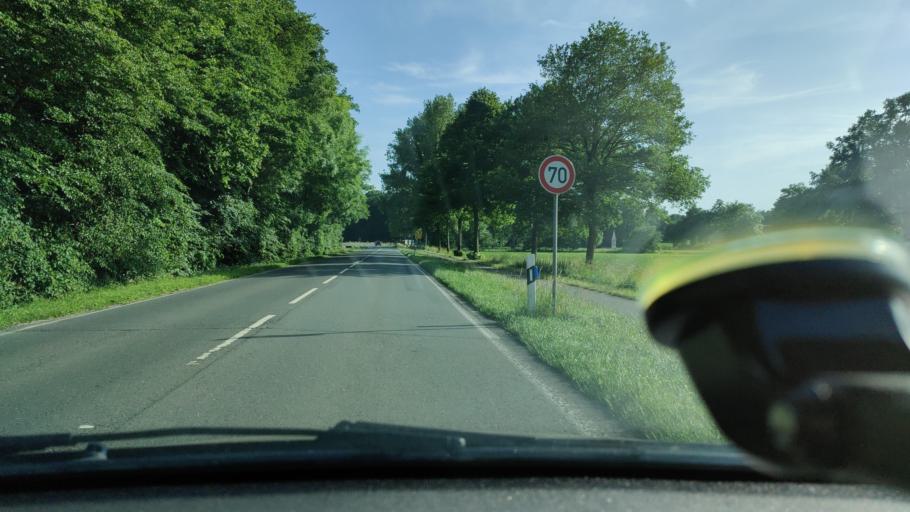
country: DE
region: North Rhine-Westphalia
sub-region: Regierungsbezirk Munster
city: Coesfeld
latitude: 51.9839
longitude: 7.1936
